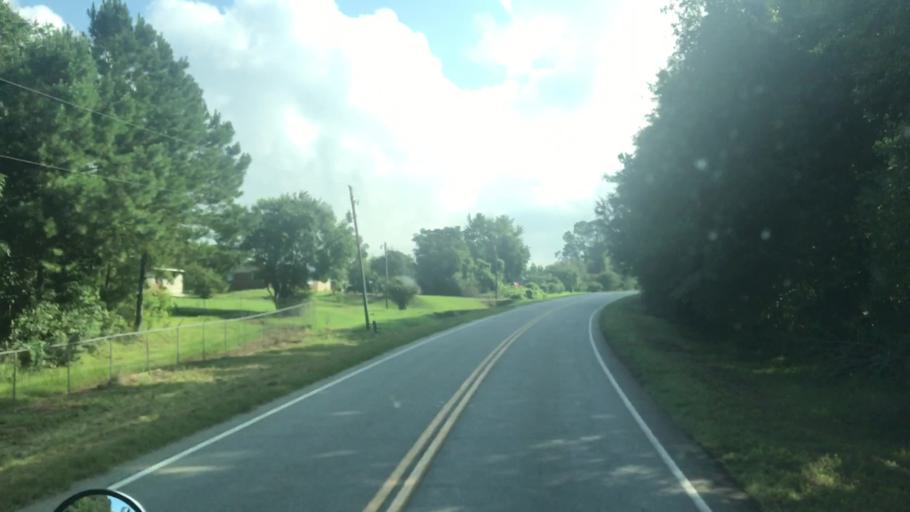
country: US
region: Florida
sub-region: Gadsden County
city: Havana
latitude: 30.7322
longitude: -84.4849
